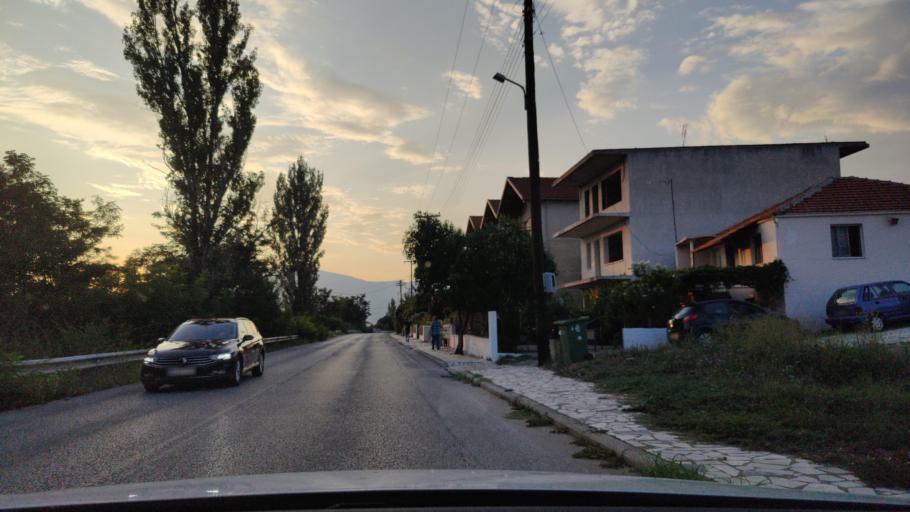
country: GR
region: Central Macedonia
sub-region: Nomos Serron
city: Sidirokastro
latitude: 41.2412
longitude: 23.3864
